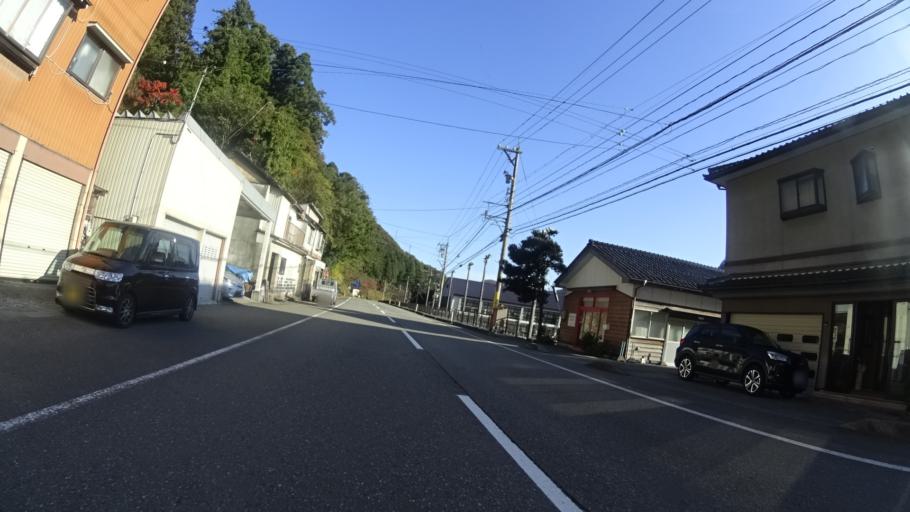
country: JP
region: Fukui
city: Maruoka
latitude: 36.2360
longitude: 136.3660
